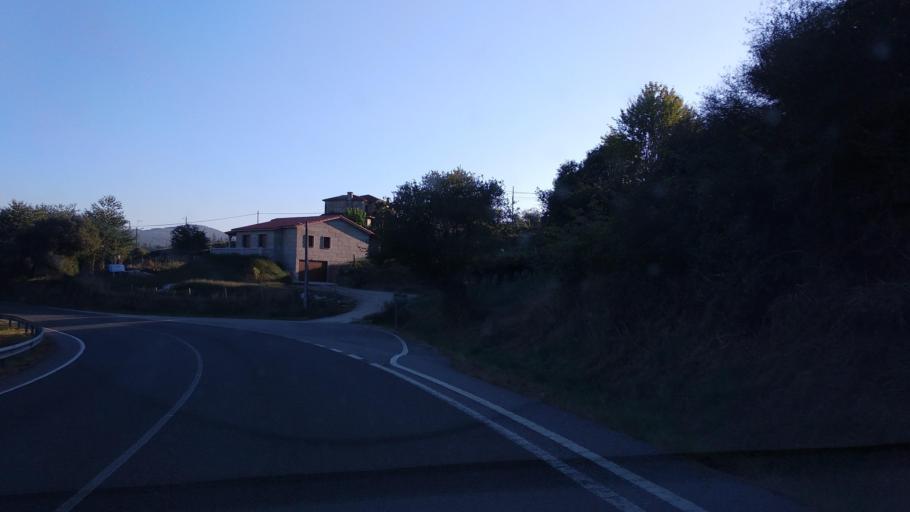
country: ES
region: Galicia
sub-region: Provincia de Pontevedra
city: Ponte Caldelas
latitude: 42.3559
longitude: -8.5426
